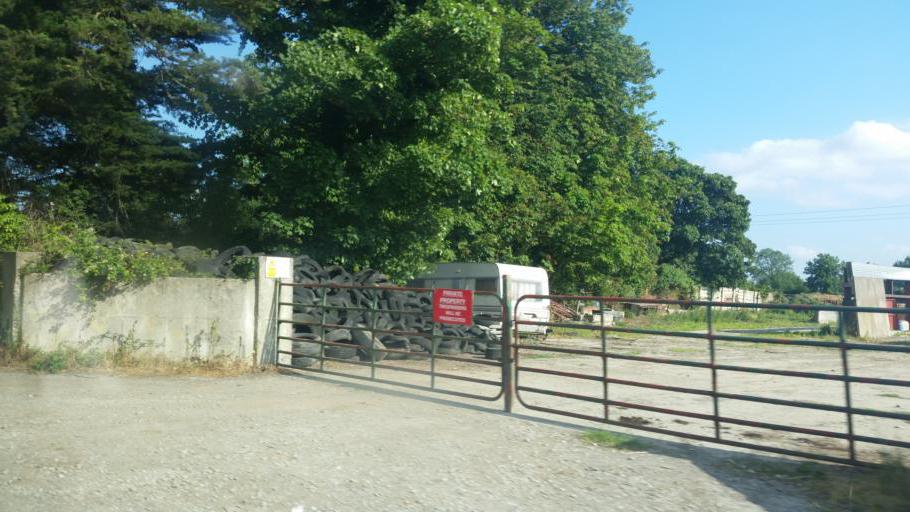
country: IE
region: Leinster
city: Hartstown
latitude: 53.4374
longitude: -6.4357
